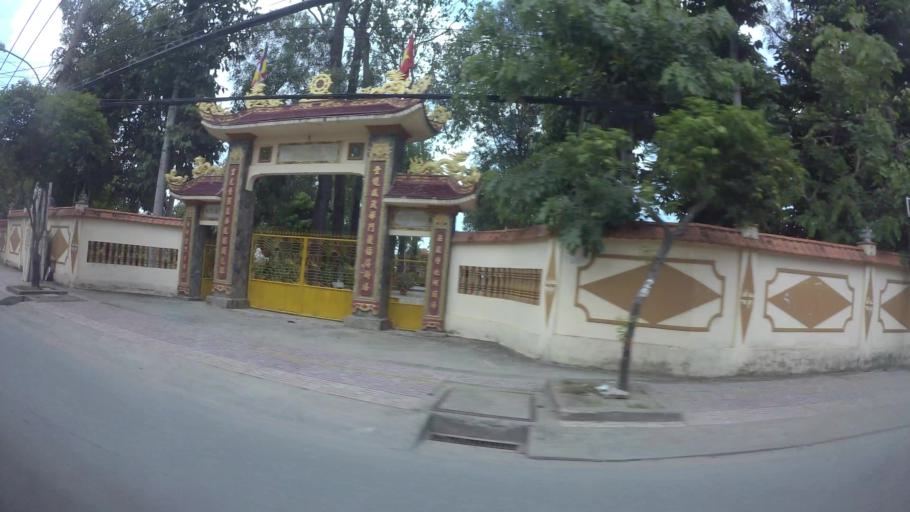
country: VN
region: Ho Chi Minh City
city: Quan Chin
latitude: 10.8324
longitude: 106.7838
